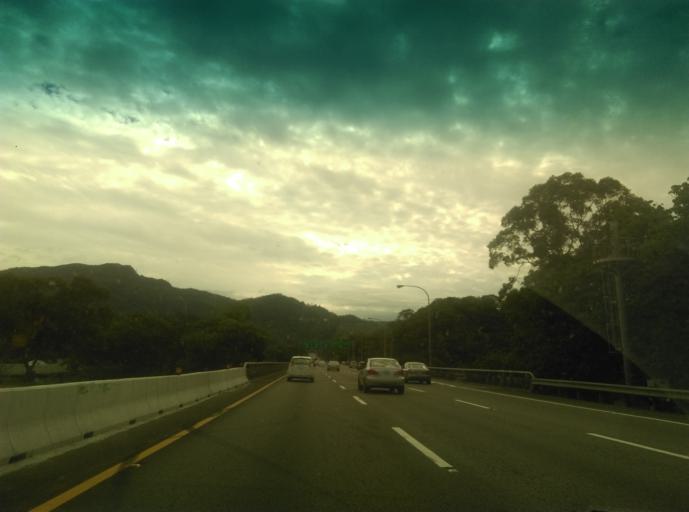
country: TW
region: Taipei
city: Taipei
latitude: 25.0068
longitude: 121.5958
